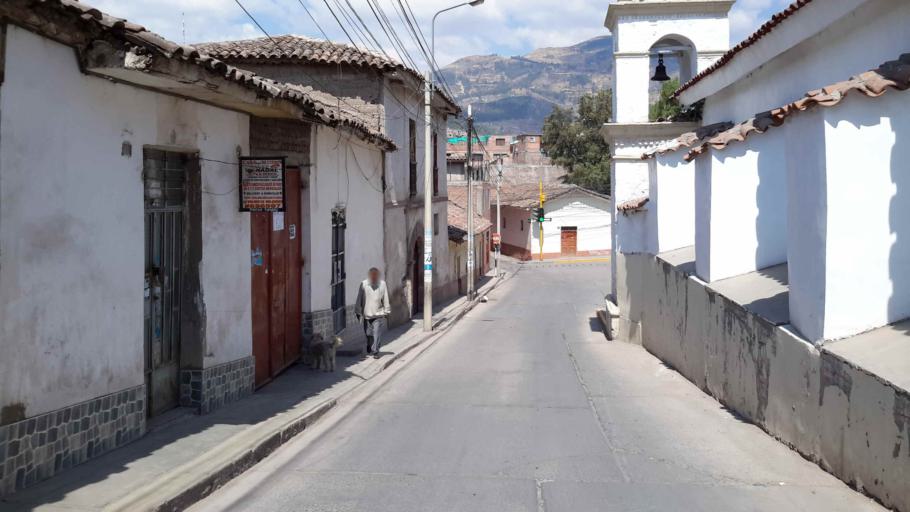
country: PE
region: Ayacucho
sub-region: Provincia de Huamanga
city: Ayacucho
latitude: -13.1622
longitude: -74.2232
